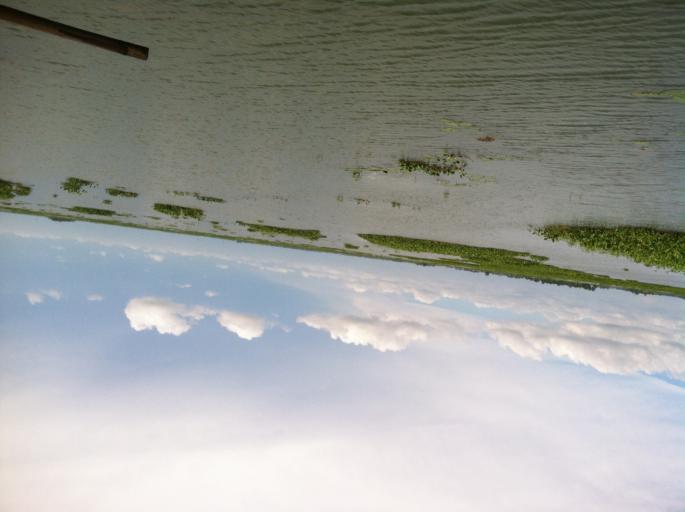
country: BD
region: Sylhet
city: Baniachang
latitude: 24.5870
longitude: 91.3584
